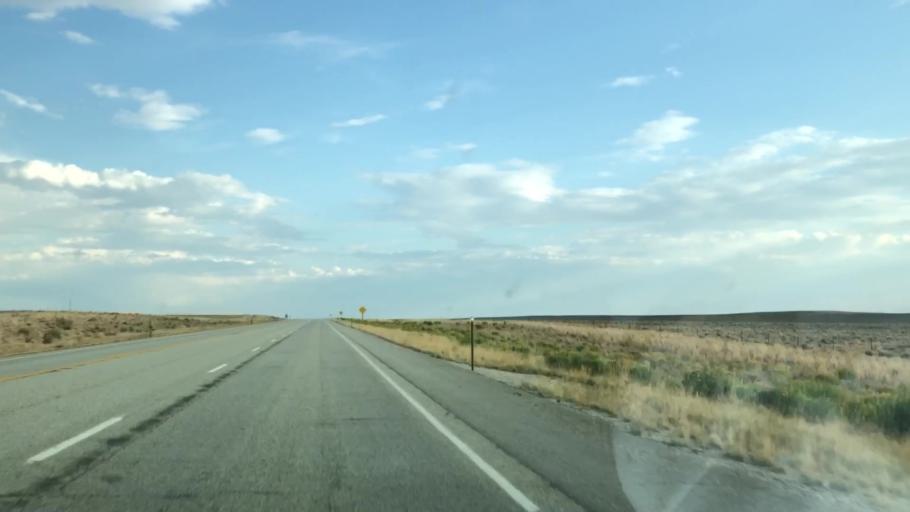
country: US
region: Wyoming
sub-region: Sweetwater County
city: North Rock Springs
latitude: 42.2680
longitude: -109.4770
